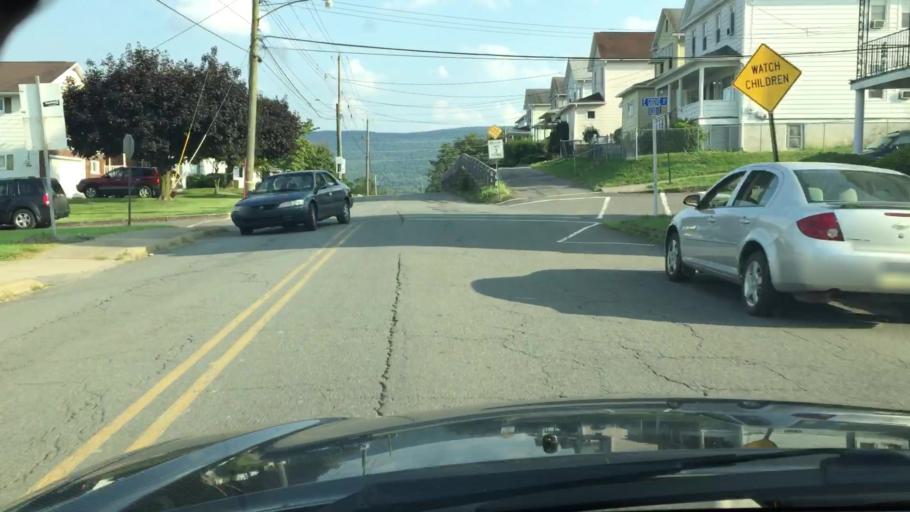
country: US
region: Pennsylvania
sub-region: Luzerne County
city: Nanticoke
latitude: 41.1993
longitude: -75.9899
